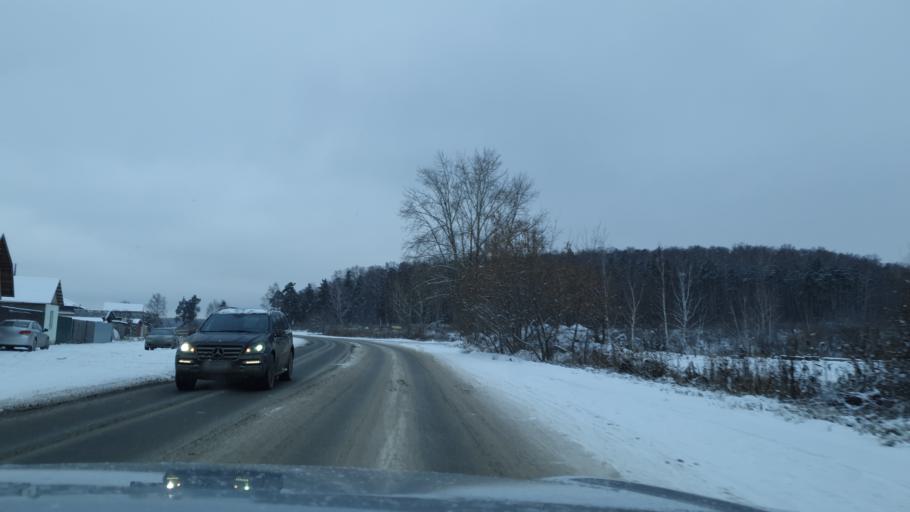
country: RU
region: Sverdlovsk
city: Istok
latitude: 56.7793
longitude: 60.7406
